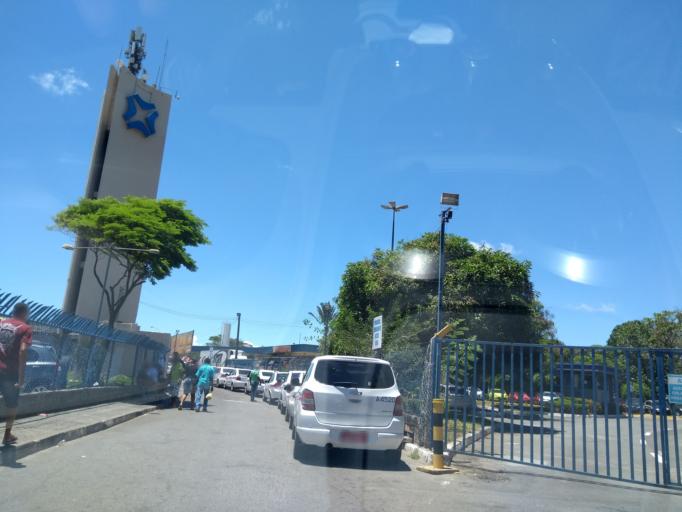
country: BR
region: Bahia
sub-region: Salvador
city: Salvador
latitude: -12.9780
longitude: -38.4644
